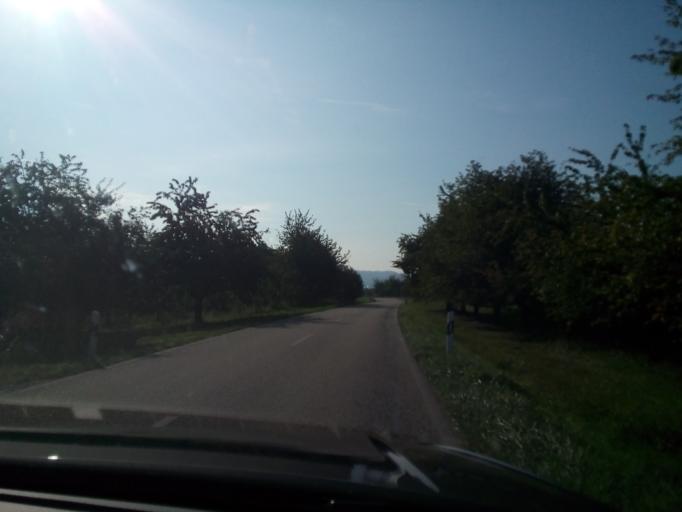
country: DE
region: Baden-Wuerttemberg
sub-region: Freiburg Region
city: Haslach
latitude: 48.5700
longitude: 8.0375
